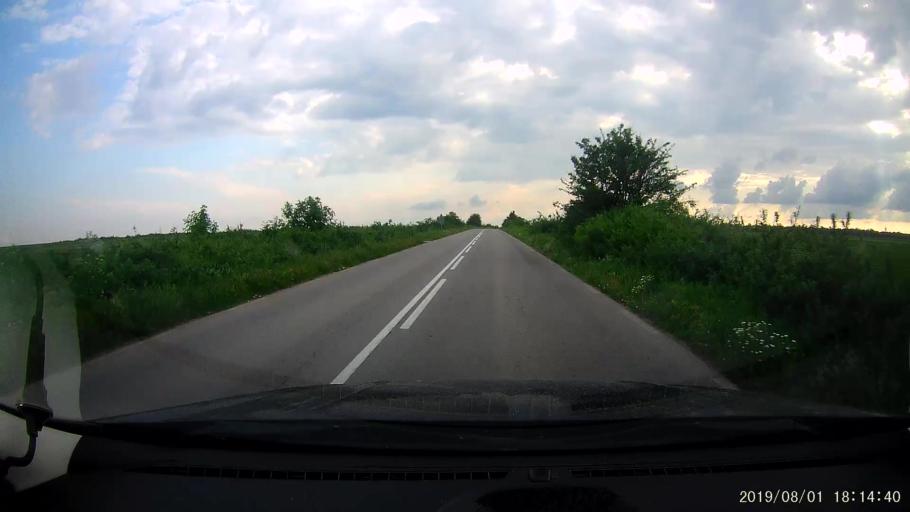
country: BG
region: Silistra
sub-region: Obshtina Dulovo
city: Dulovo
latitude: 43.7647
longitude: 27.1215
